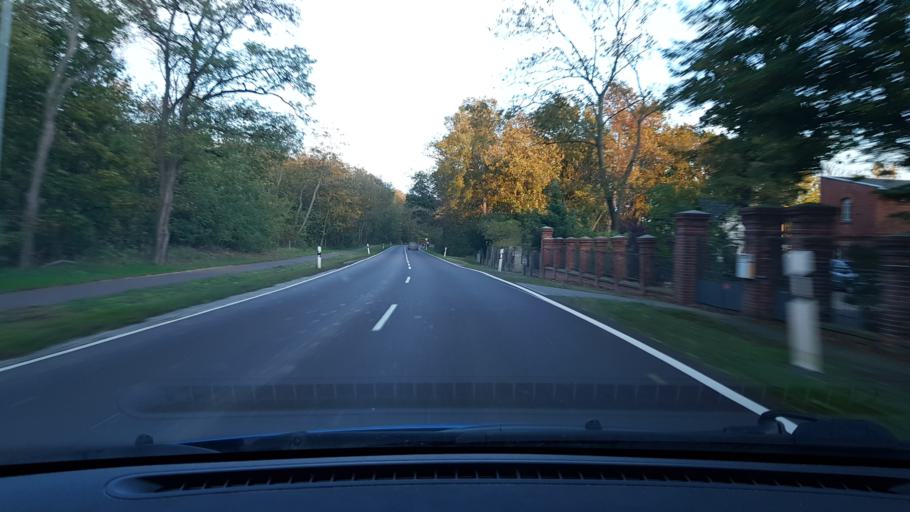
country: DE
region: Saxony-Anhalt
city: Biederitz
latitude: 52.1353
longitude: 11.7478
